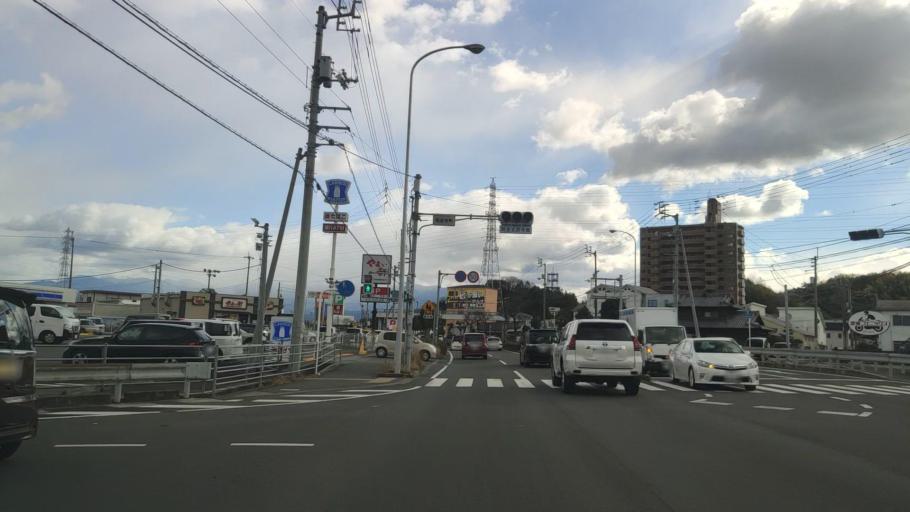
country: JP
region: Ehime
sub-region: Shikoku-chuo Shi
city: Matsuyama
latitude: 33.8219
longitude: 132.7868
